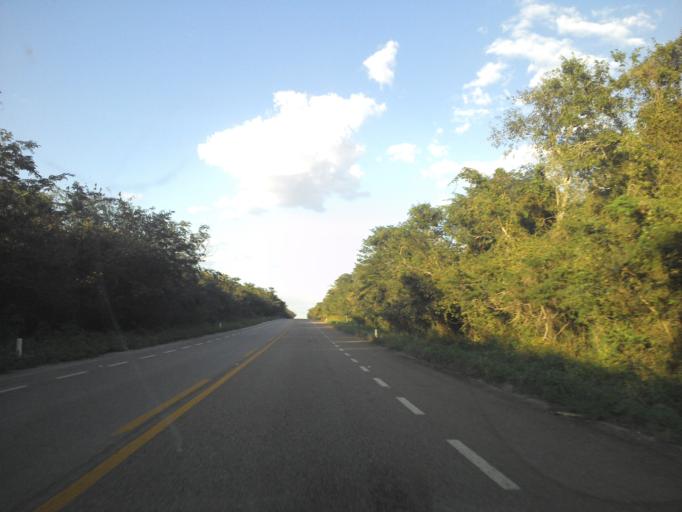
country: MX
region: Yucatan
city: Santa Elena
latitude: 20.3495
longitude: -89.7224
